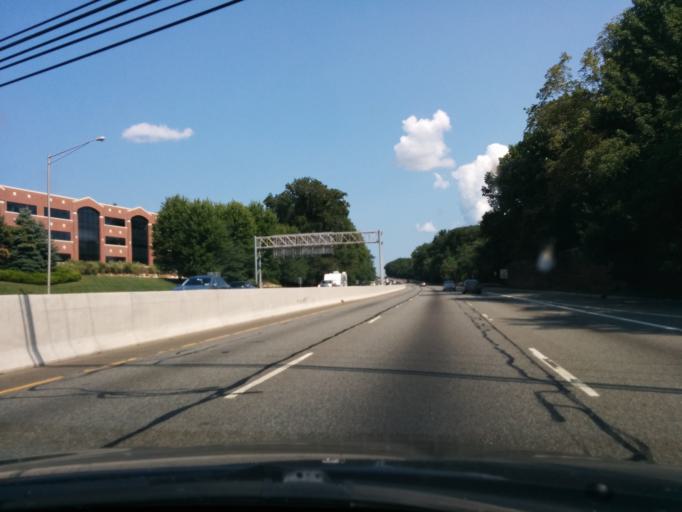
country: US
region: New Jersey
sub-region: Bergen County
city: Saddle River
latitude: 41.0337
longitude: -74.1115
